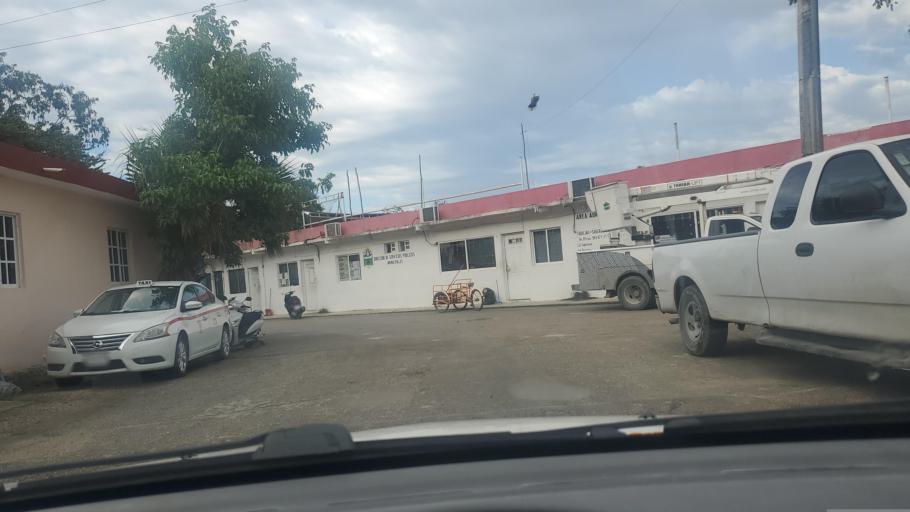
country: MX
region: Quintana Roo
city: Tulum
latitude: 20.2111
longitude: -87.4677
